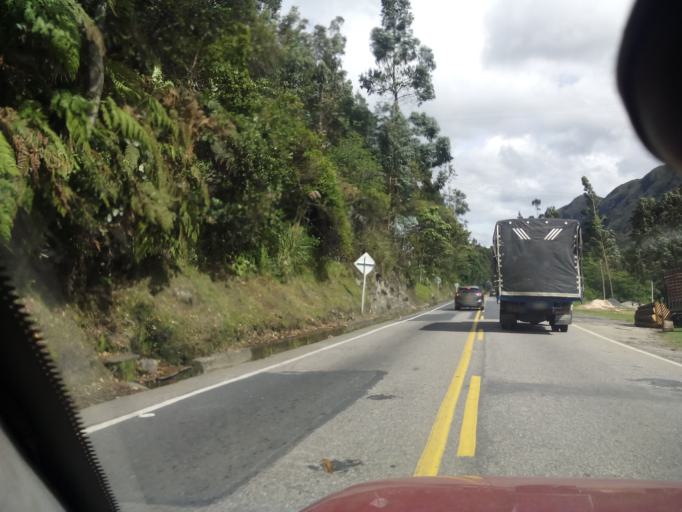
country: CO
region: Boyaca
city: Arcabuco
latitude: 5.7343
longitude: -73.4090
